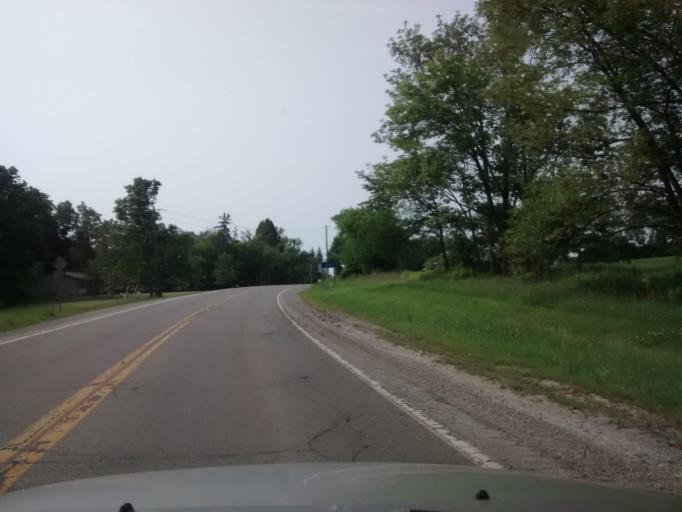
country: CA
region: Ontario
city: Ancaster
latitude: 43.0164
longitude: -79.8869
